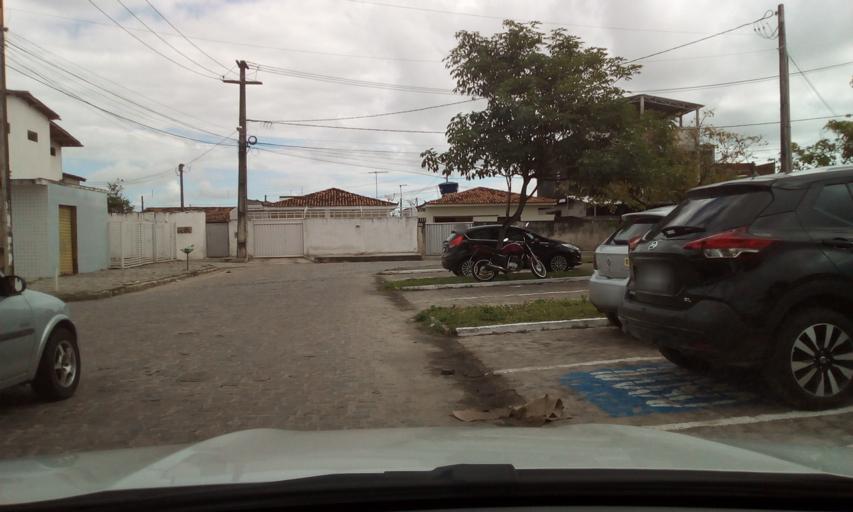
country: BR
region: Paraiba
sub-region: Joao Pessoa
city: Joao Pessoa
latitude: -7.1803
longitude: -34.8766
